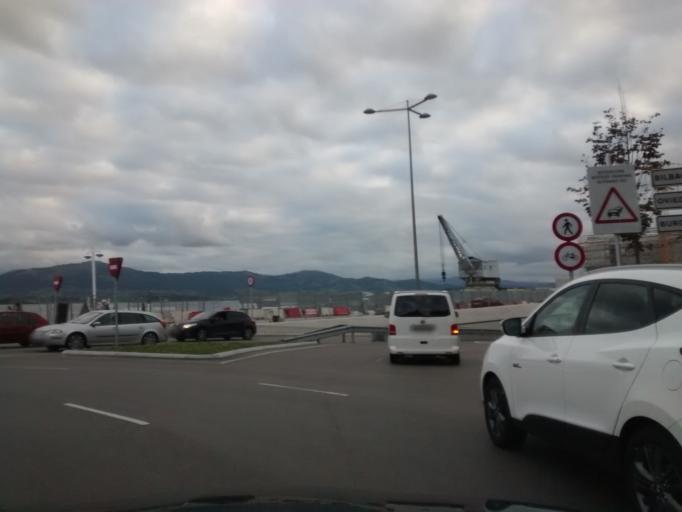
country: ES
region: Cantabria
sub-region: Provincia de Cantabria
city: Santander
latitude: 43.4618
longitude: -3.8024
